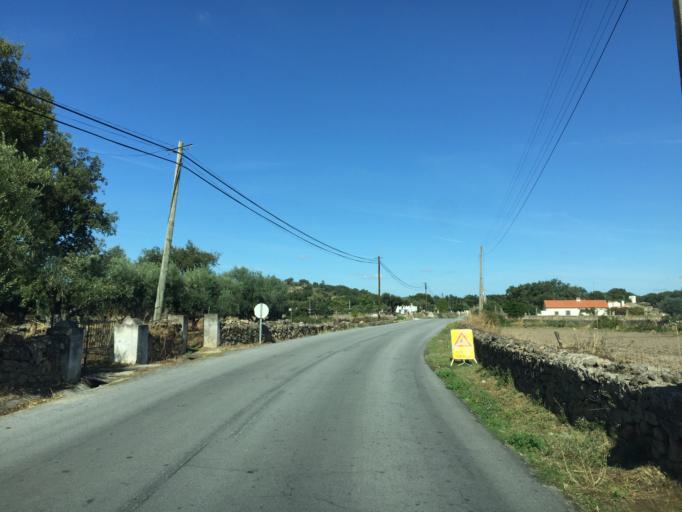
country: PT
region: Portalegre
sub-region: Marvao
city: Marvao
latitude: 39.4263
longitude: -7.3548
